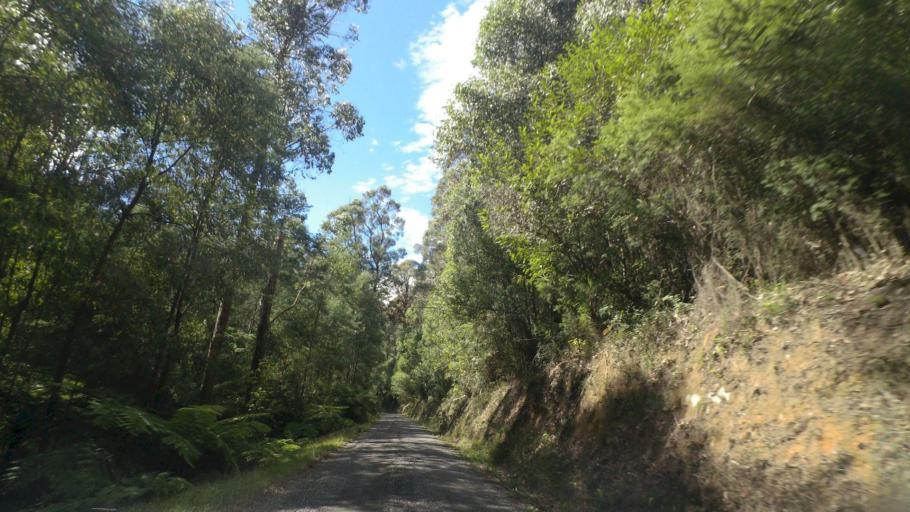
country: AU
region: Victoria
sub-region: Cardinia
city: Bunyip
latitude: -37.9587
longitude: 145.8185
